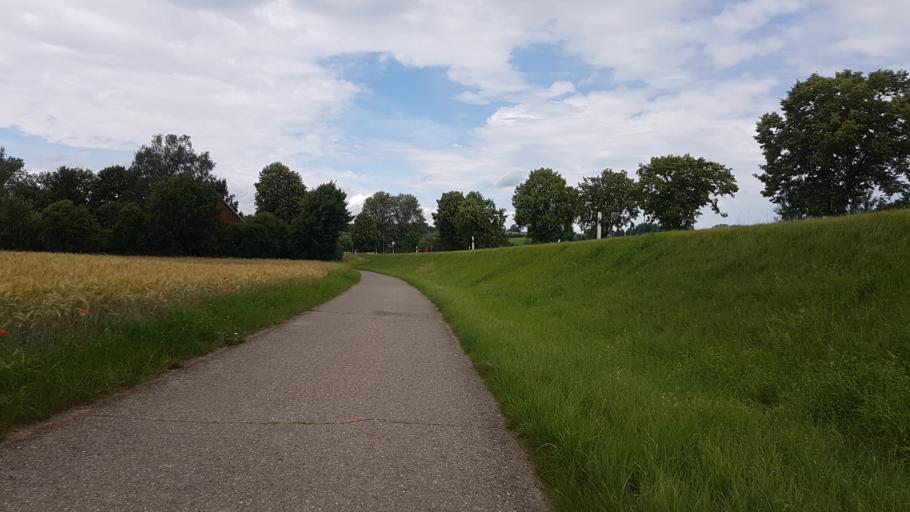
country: DE
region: Baden-Wuerttemberg
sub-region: Tuebingen Region
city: Mengen
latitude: 48.0607
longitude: 9.3463
